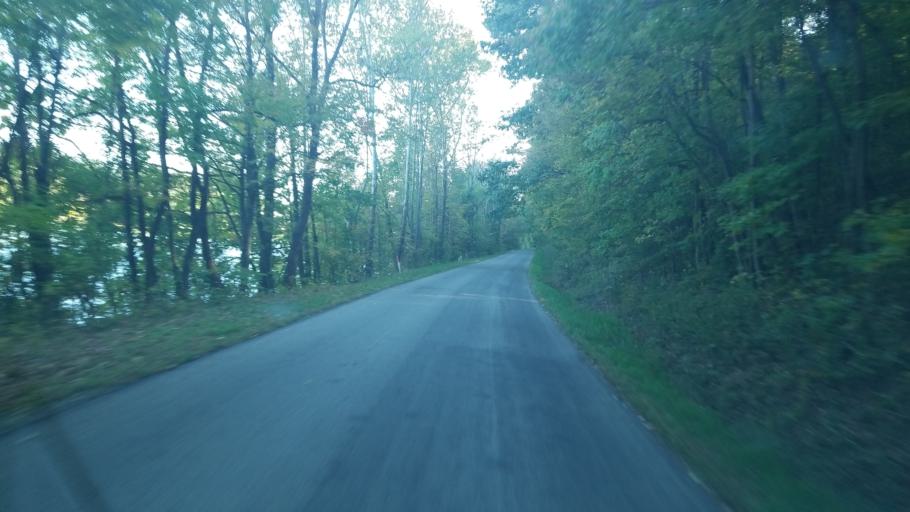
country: US
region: Ohio
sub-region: Wayne County
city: Wooster
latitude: 40.8758
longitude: -82.0121
